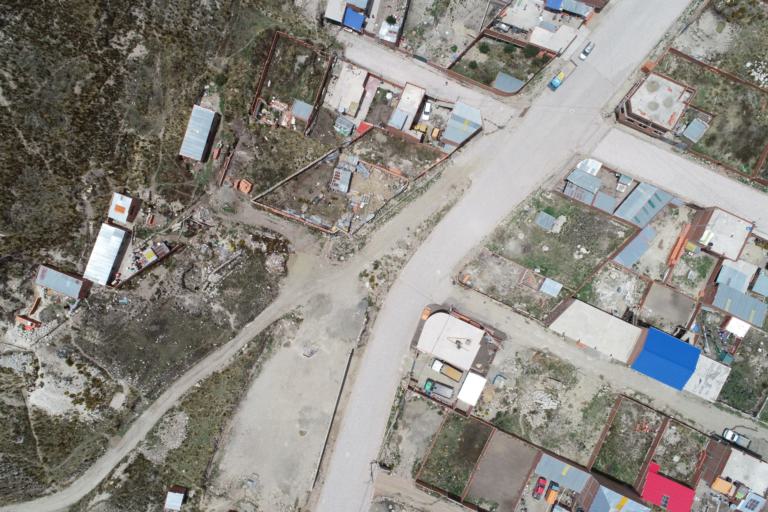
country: BO
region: La Paz
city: La Paz
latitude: -16.4394
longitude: -68.1423
